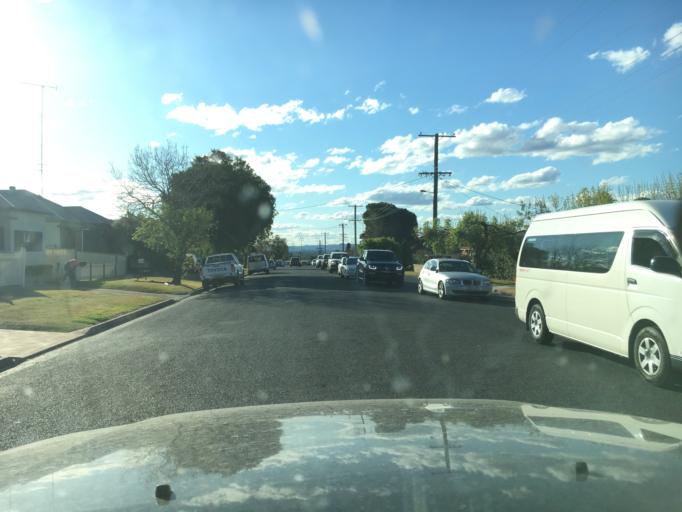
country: AU
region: New South Wales
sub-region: Maitland Municipality
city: East Maitland
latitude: -32.7560
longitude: 151.5853
